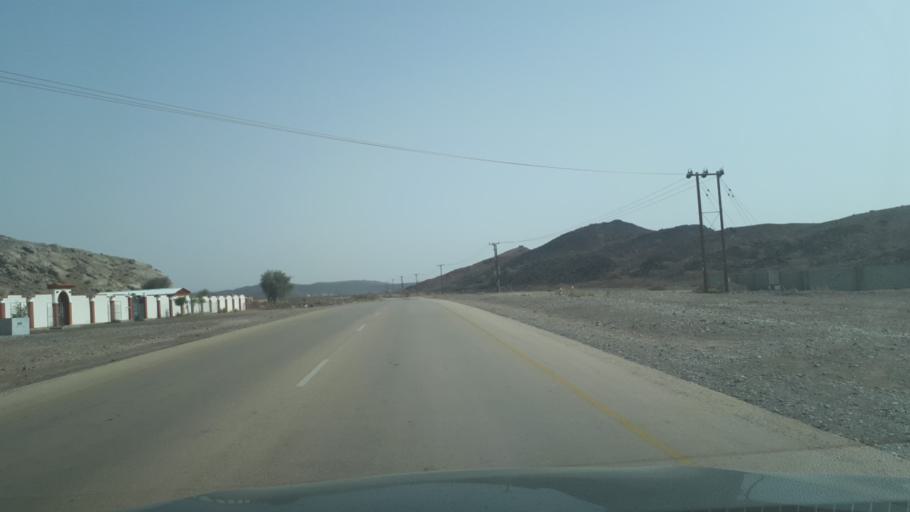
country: OM
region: Az Zahirah
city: `Ibri
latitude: 23.1566
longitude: 56.9108
